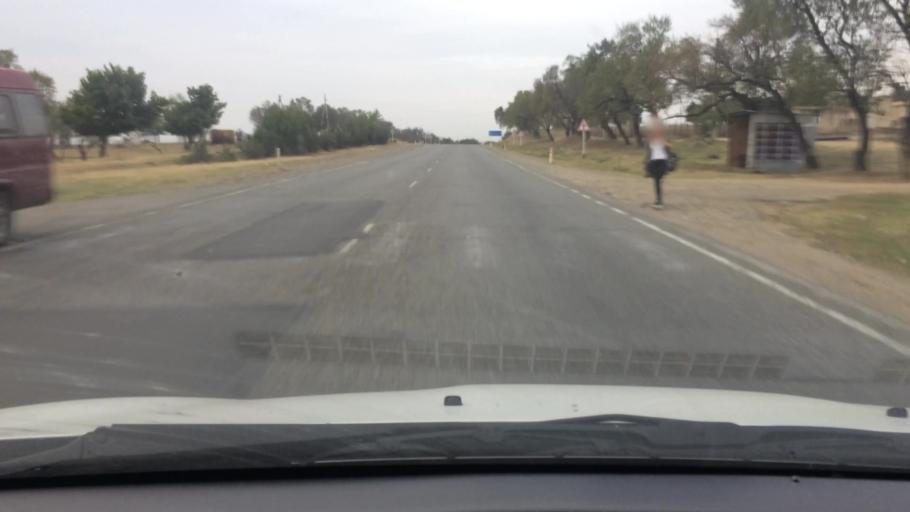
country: GE
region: T'bilisi
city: Tbilisi
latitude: 41.6394
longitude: 44.8315
